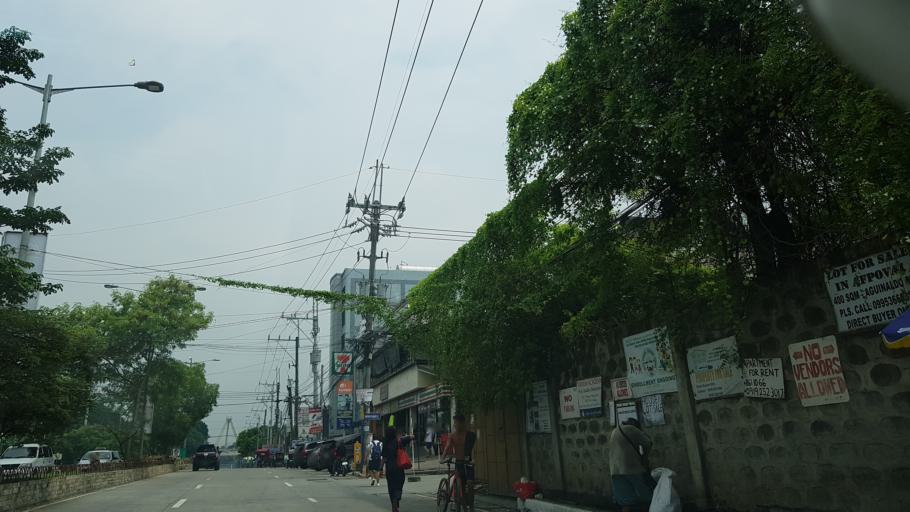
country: PH
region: Metro Manila
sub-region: Makati City
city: Makati City
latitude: 14.5259
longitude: 121.0431
